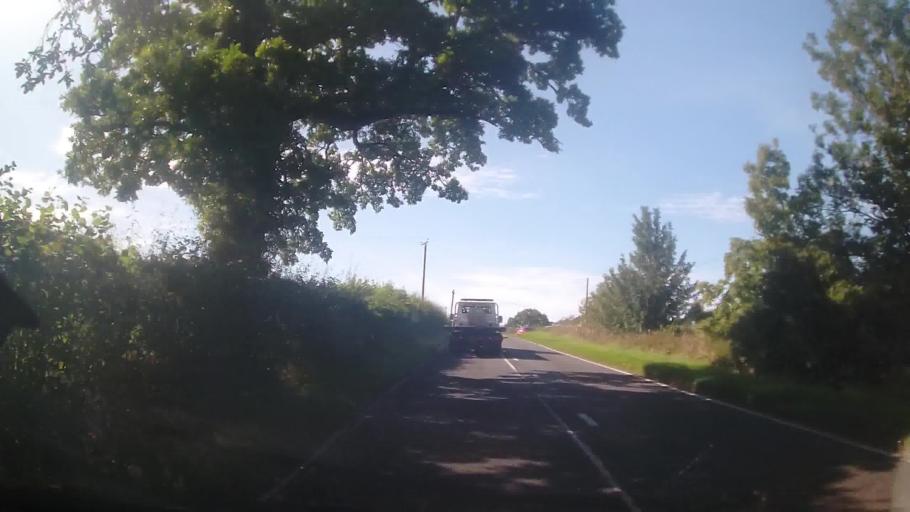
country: GB
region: Wales
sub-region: Sir Powys
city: Llandrindod Wells
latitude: 52.2825
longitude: -3.3783
